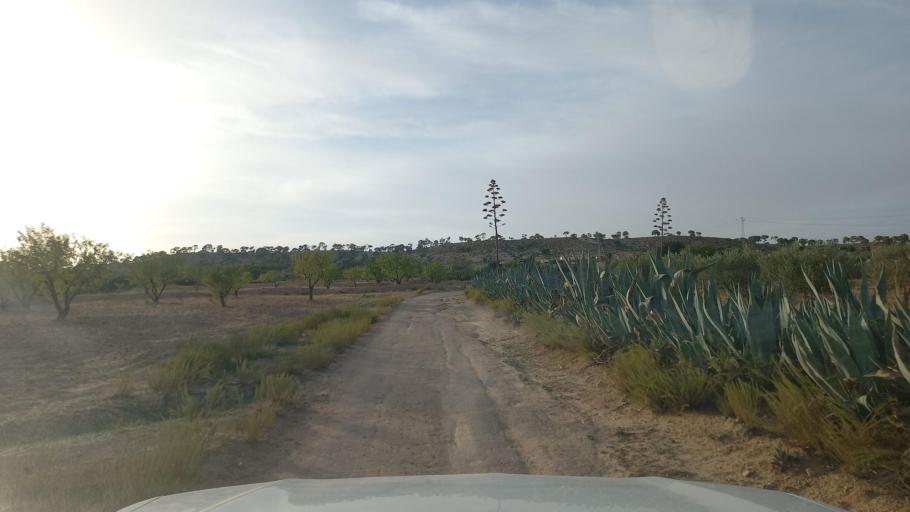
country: TN
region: Al Qasrayn
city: Sbiba
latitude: 35.4045
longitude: 8.8992
